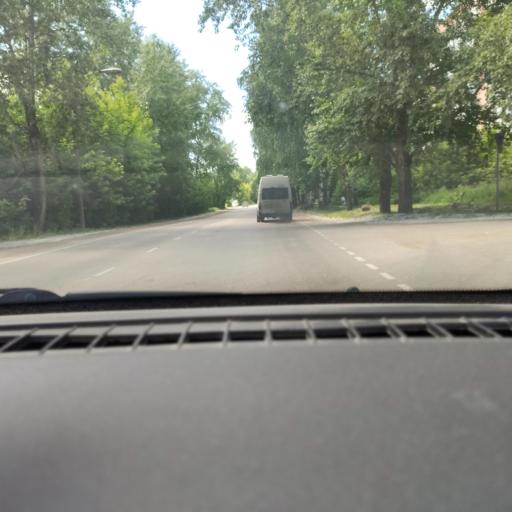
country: RU
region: Perm
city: Krasnokamsk
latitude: 58.0771
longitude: 55.7151
